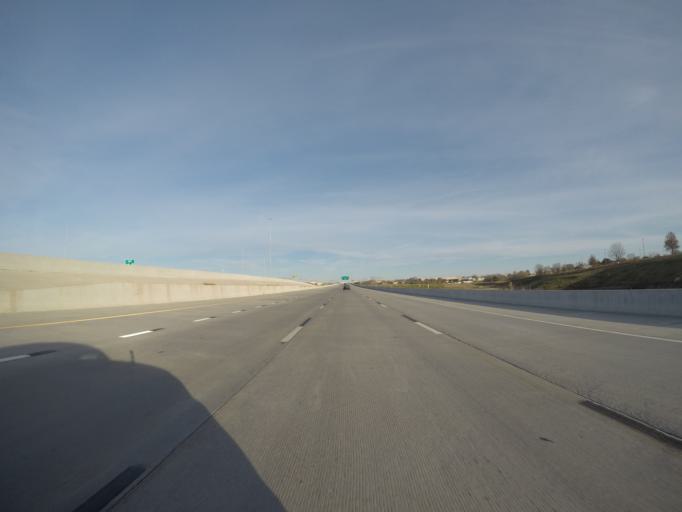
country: US
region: Kansas
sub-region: Johnson County
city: Lenexa
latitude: 38.9420
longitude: -94.7675
